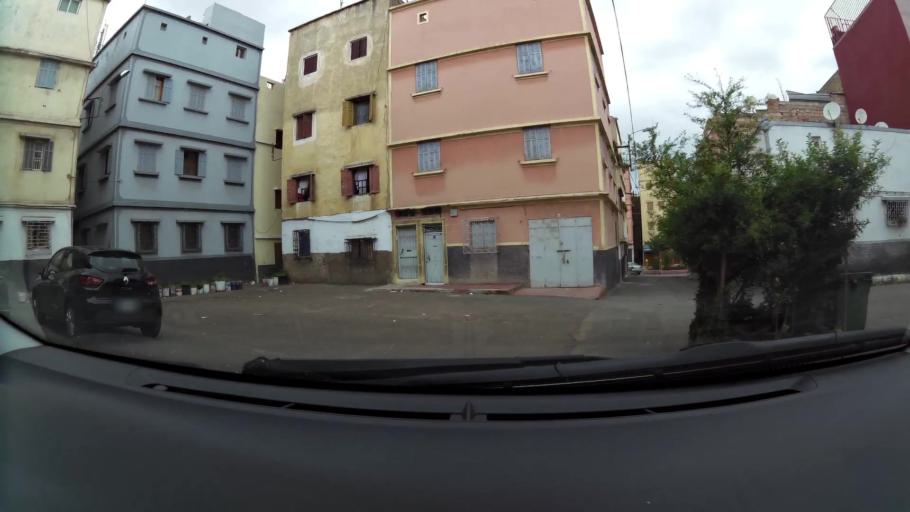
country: MA
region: Grand Casablanca
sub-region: Casablanca
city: Casablanca
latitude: 33.5635
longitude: -7.5671
